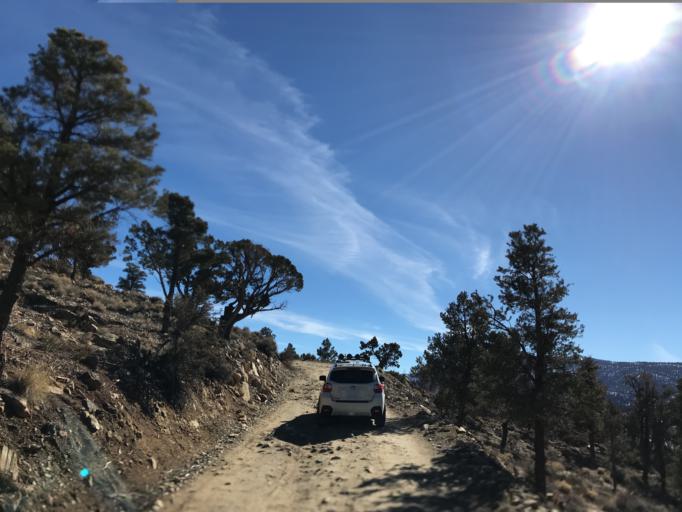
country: US
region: California
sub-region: San Bernardino County
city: Big Bear City
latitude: 34.2734
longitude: -116.7861
